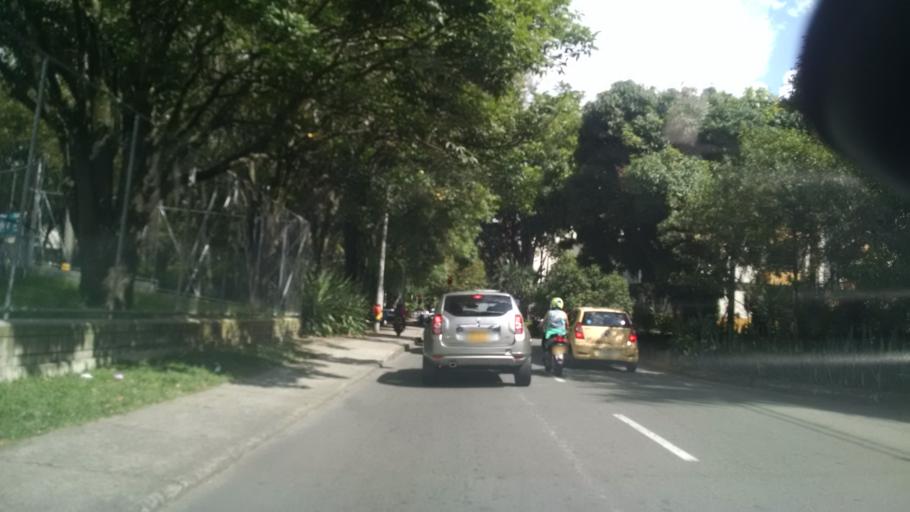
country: CO
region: Antioquia
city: Medellin
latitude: 6.2542
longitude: -75.5925
